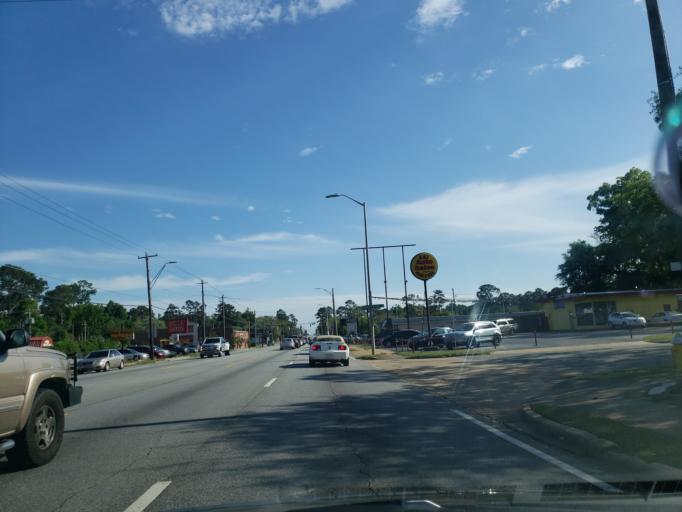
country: US
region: Georgia
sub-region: Dougherty County
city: Albany
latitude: 31.5919
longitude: -84.1761
